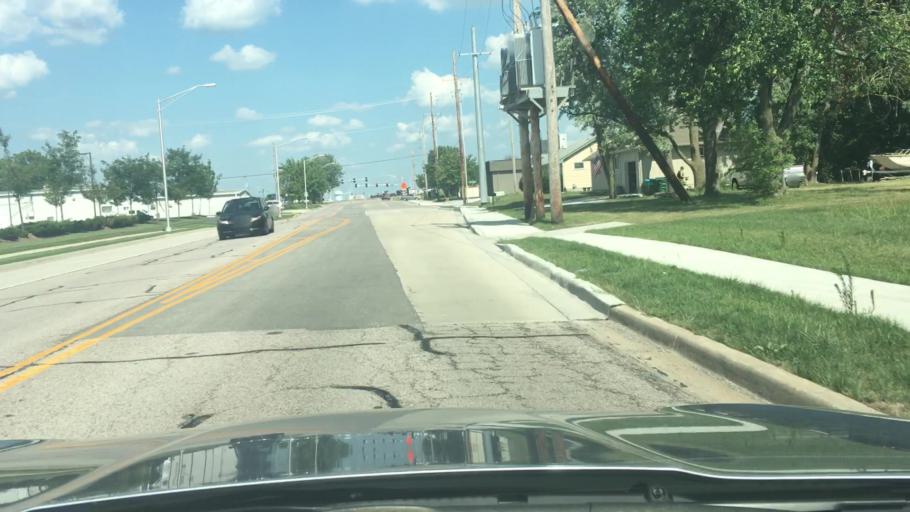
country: US
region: Missouri
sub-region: Jackson County
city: Lees Summit
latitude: 38.8961
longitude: -94.3788
